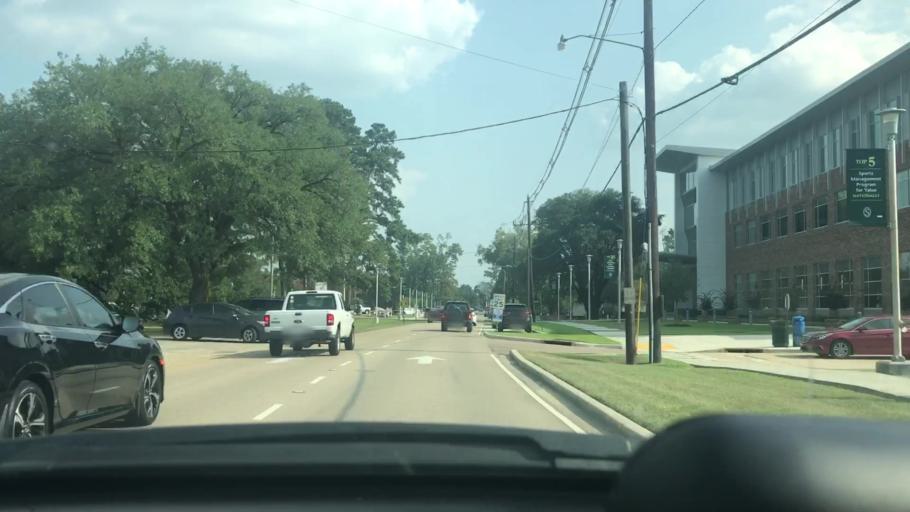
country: US
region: Louisiana
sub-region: Tangipahoa Parish
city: Hammond
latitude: 30.5117
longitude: -90.4647
